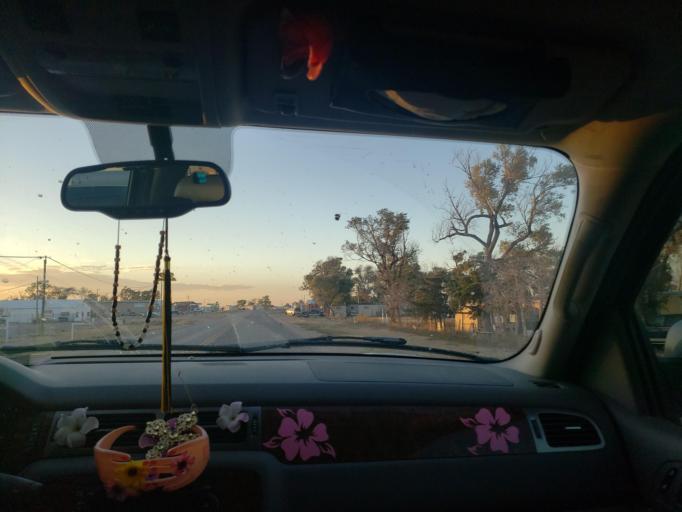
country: US
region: Kansas
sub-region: Finney County
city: Garden City
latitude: 37.9868
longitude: -100.9115
